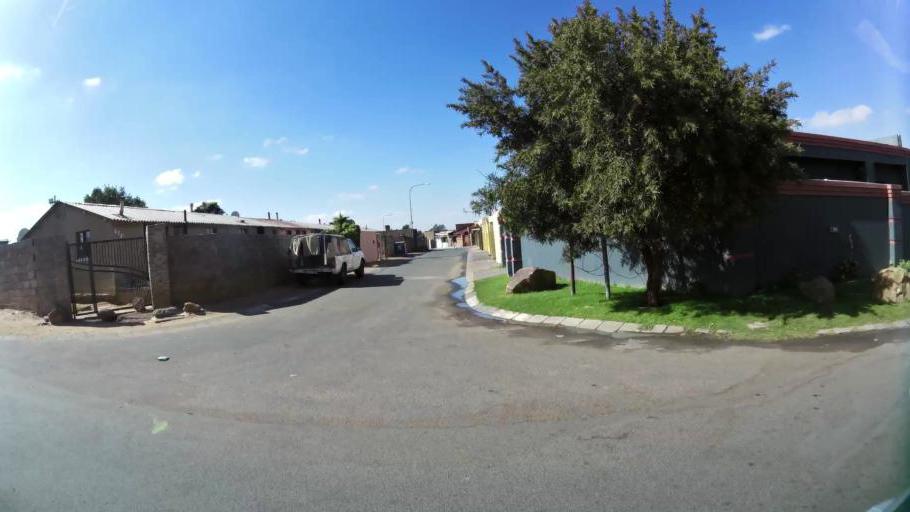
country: ZA
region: Gauteng
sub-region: City of Johannesburg Metropolitan Municipality
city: Roodepoort
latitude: -26.2184
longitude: 27.8953
